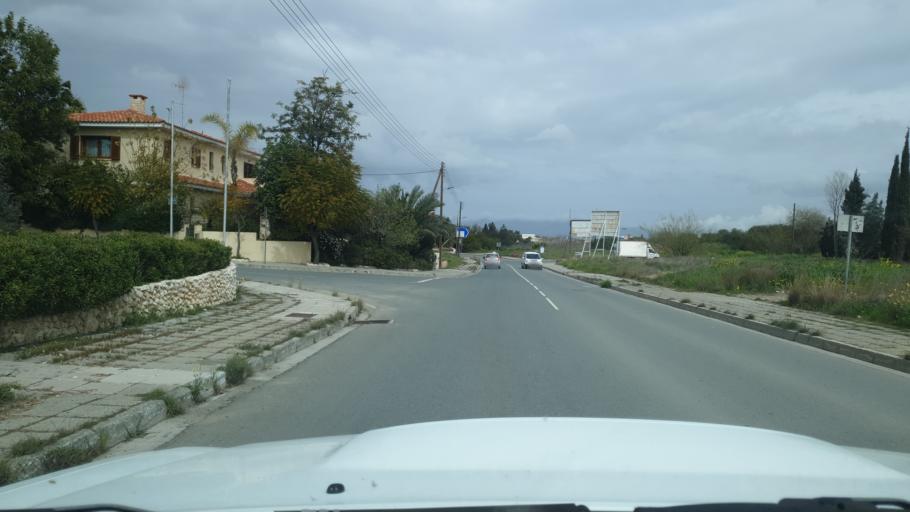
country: CY
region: Lefkosia
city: Tseri
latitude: 35.1046
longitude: 33.3560
